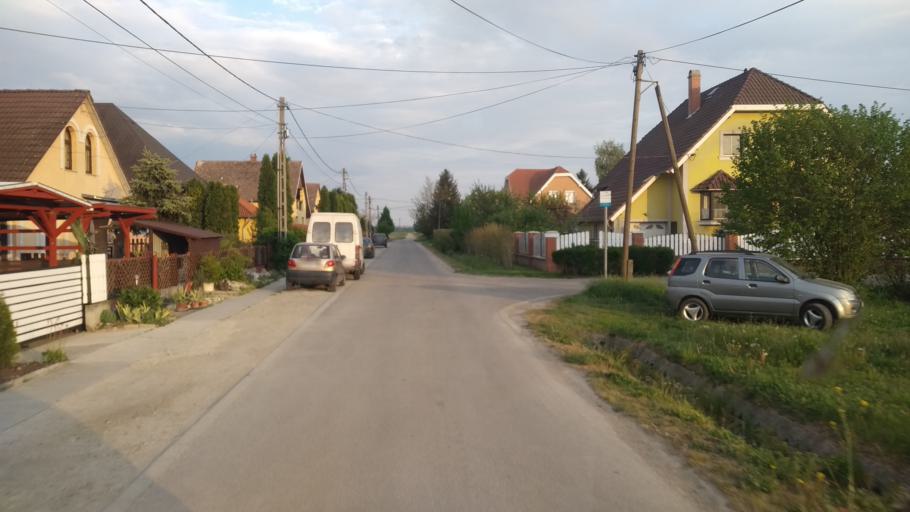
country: HU
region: Pest
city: Tahitotfalu
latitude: 47.7518
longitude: 19.0999
